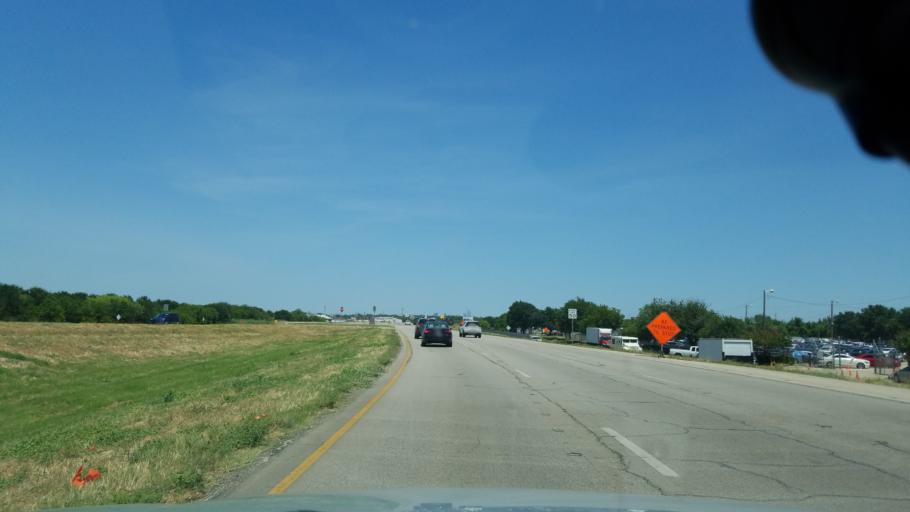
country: US
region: Texas
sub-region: Dallas County
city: Grand Prairie
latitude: 32.7474
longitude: -96.9491
